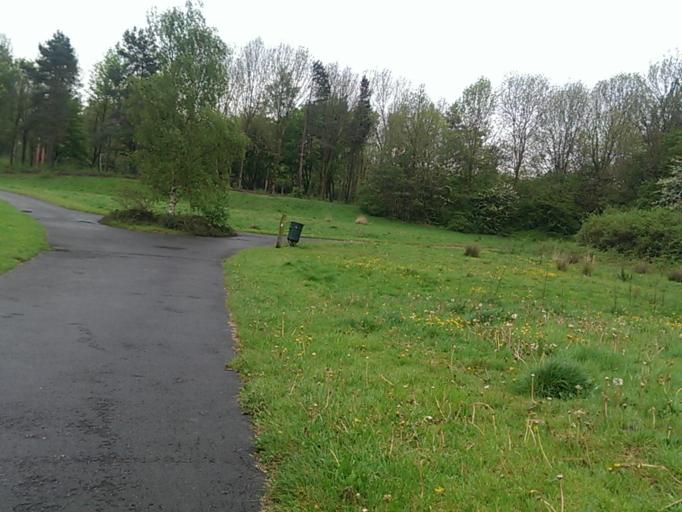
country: GB
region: England
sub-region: Warrington
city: Culcheth
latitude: 53.4260
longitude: -2.5135
